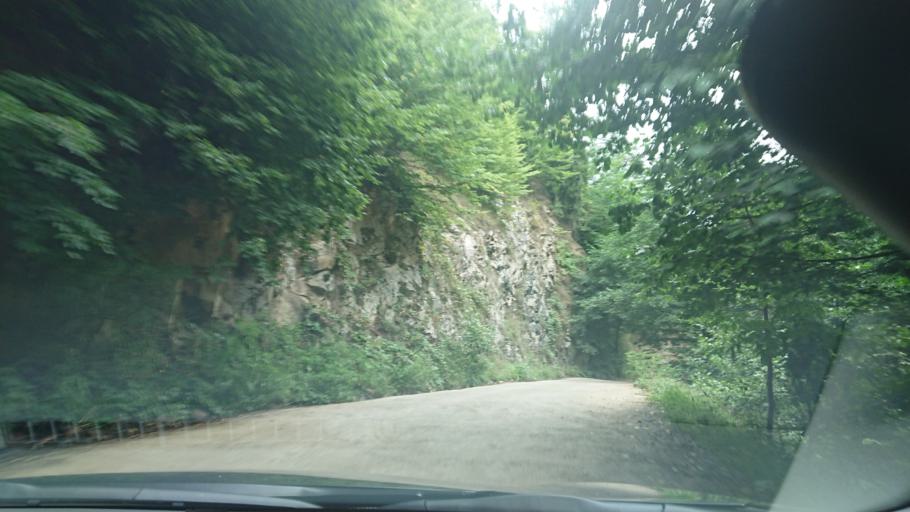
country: TR
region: Gumushane
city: Kurtun
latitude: 40.6764
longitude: 39.0426
